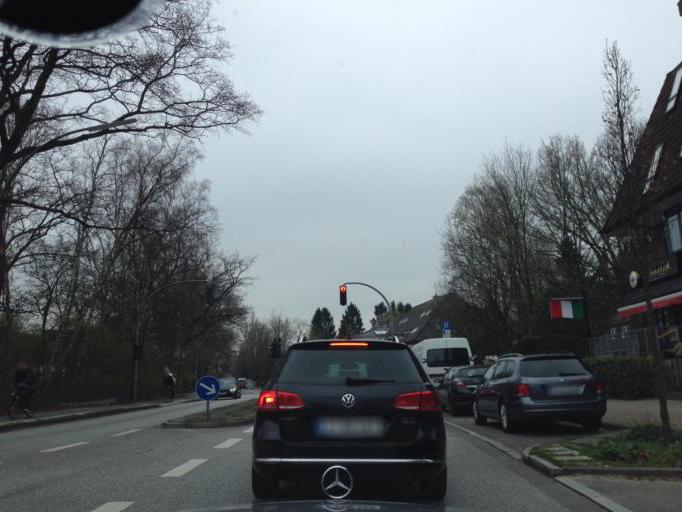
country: DE
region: Hamburg
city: Sasel
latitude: 53.6495
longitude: 10.1175
